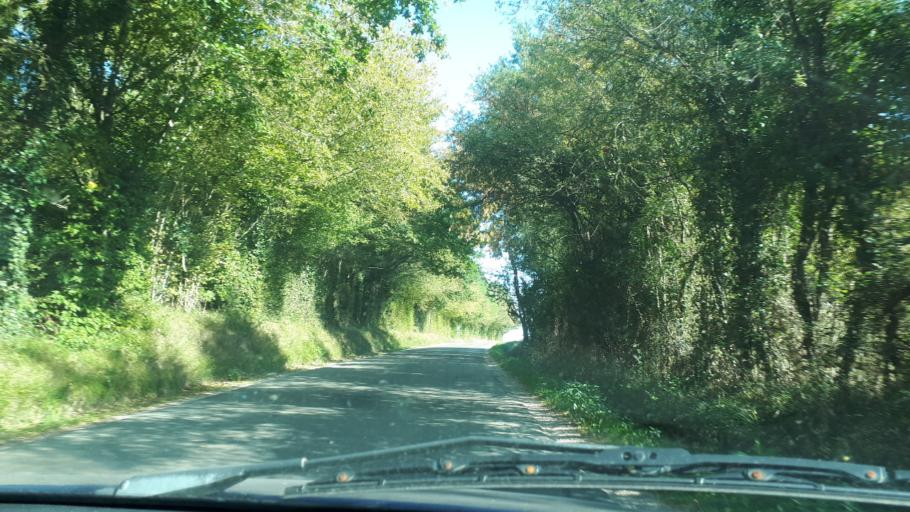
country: FR
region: Centre
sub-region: Departement du Loir-et-Cher
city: Mondoubleau
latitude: 47.9859
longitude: 0.9224
